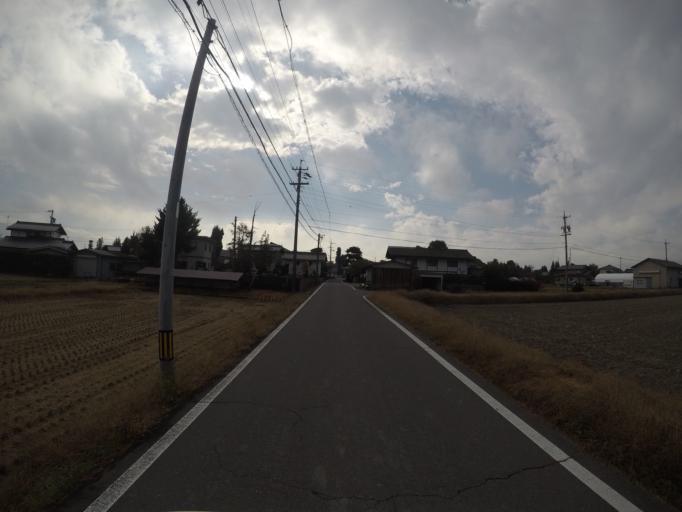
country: JP
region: Nagano
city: Matsumoto
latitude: 36.2205
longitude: 137.9000
